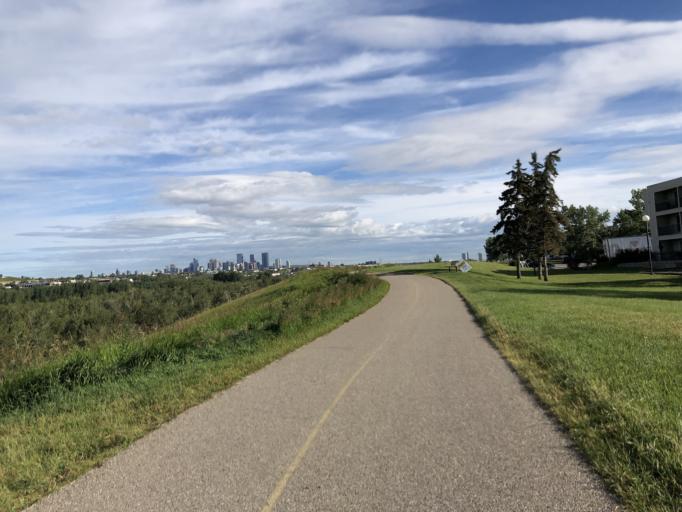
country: CA
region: Alberta
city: Calgary
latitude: 50.9944
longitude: -114.0227
